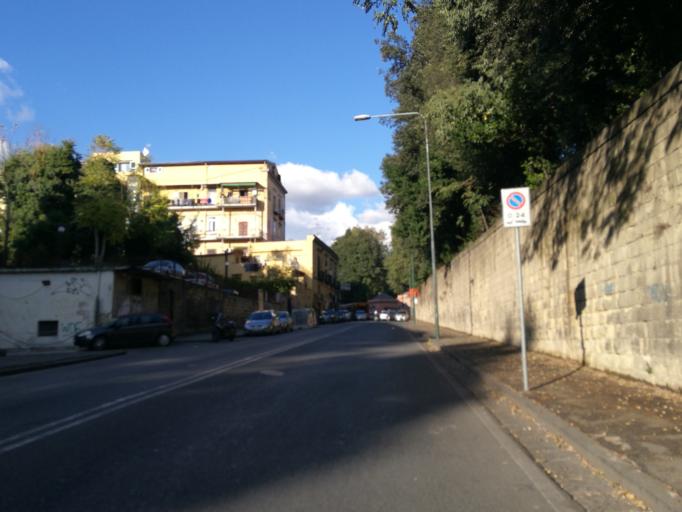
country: IT
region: Campania
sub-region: Provincia di Napoli
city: Napoli
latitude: 40.8687
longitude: 14.2499
